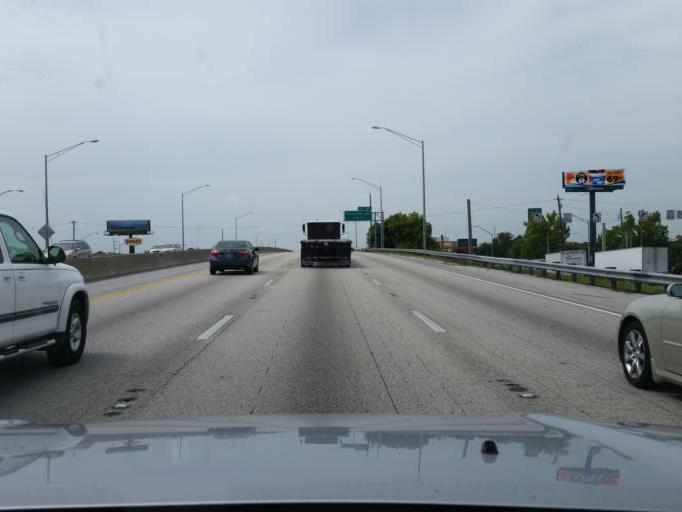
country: US
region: Florida
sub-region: Orange County
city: Eatonville
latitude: 28.6077
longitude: -81.3866
